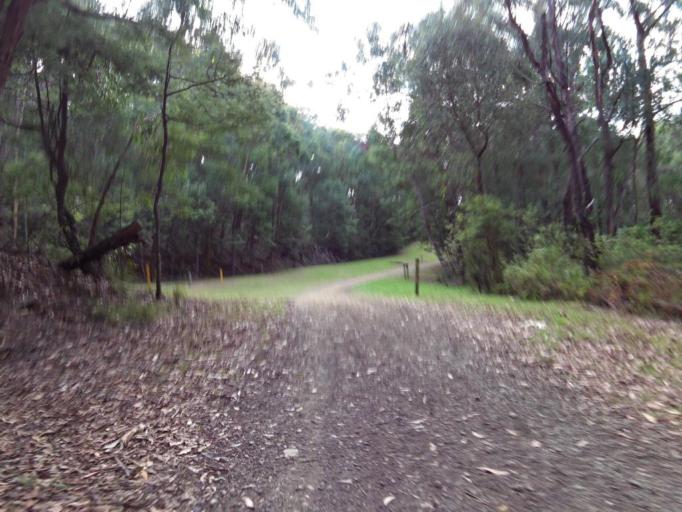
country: AU
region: Victoria
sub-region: Yarra Ranges
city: Mount Evelyn
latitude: -37.8047
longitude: 145.3917
